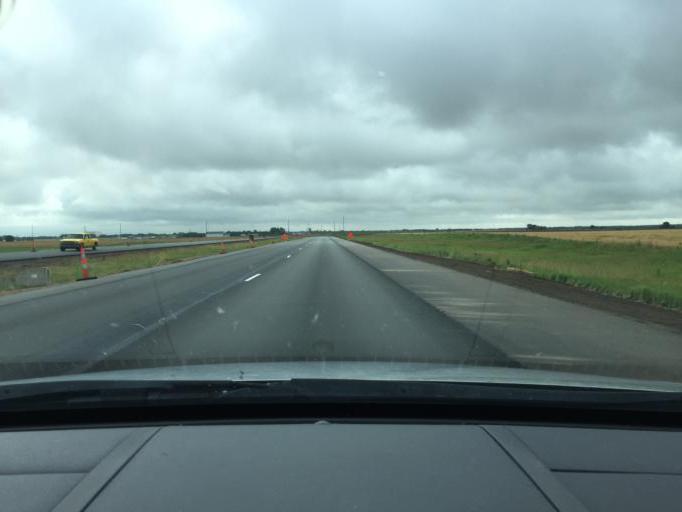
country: US
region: Kansas
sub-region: Reno County
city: South Hutchinson
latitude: 38.0137
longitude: -97.9866
